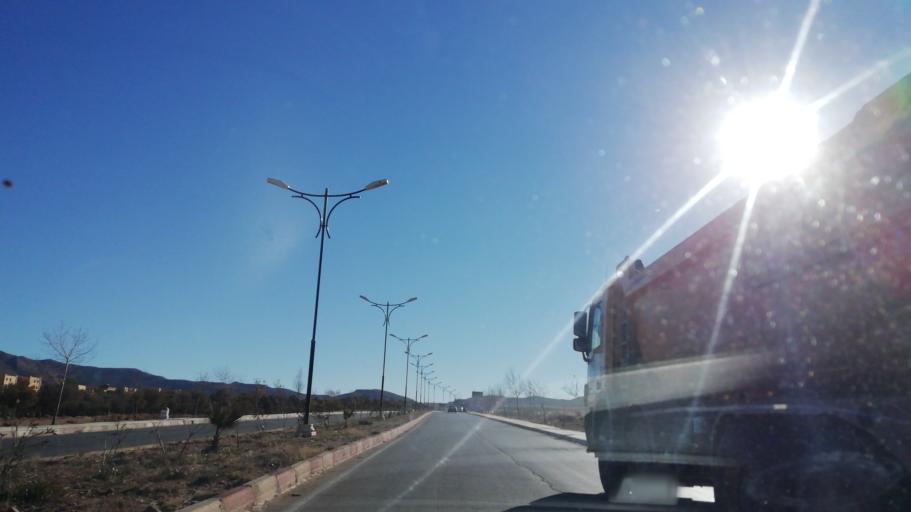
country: DZ
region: El Bayadh
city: El Bayadh
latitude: 33.6587
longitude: 1.0635
